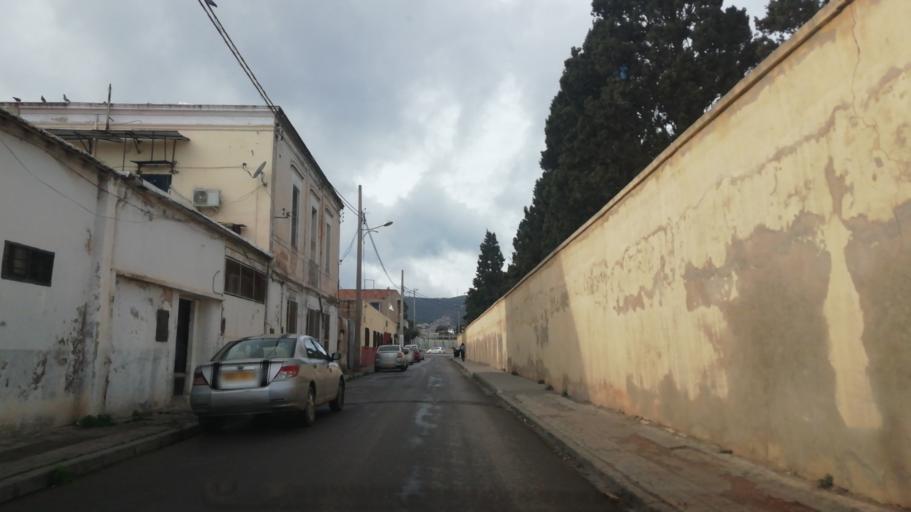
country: DZ
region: Oran
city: Oran
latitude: 35.6906
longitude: -0.6389
